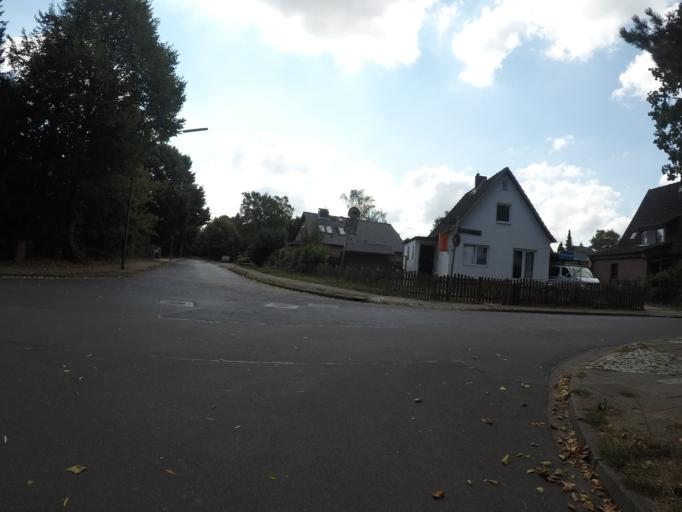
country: DE
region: Hamburg
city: Eidelstedt
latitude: 53.5815
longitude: 9.8742
